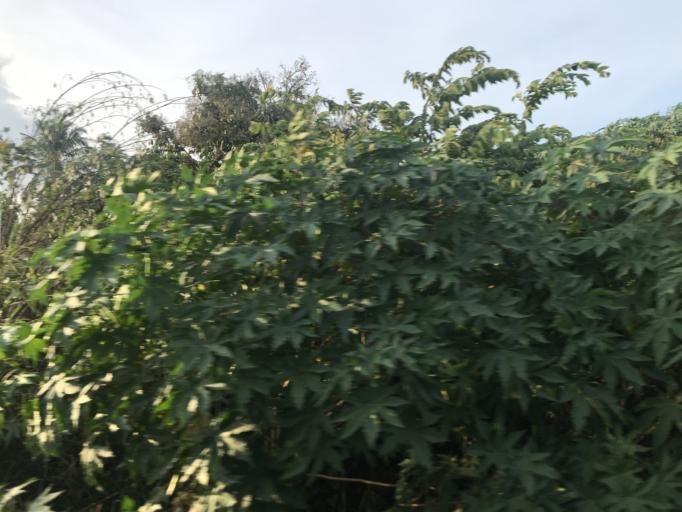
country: IN
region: Tamil Nadu
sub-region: Coimbatore
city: Coimbatore
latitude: 11.0299
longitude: 76.9819
